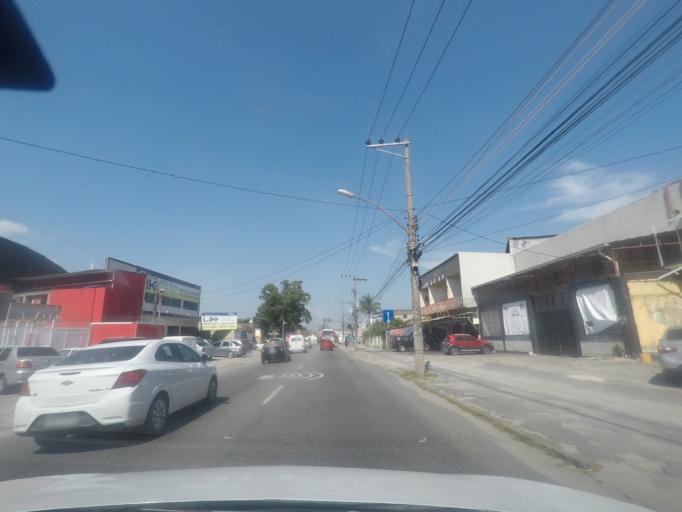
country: BR
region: Rio de Janeiro
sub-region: Nilopolis
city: Nilopolis
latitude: -22.8778
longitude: -43.4473
